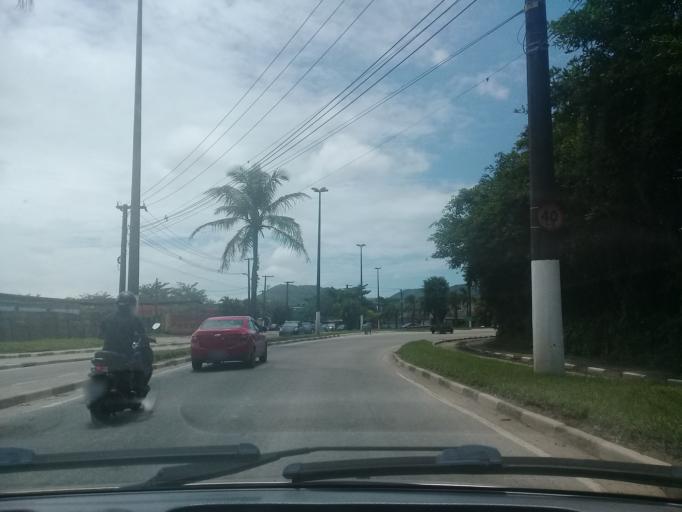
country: BR
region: Sao Paulo
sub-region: Guaruja
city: Guaruja
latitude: -23.9661
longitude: -46.2613
